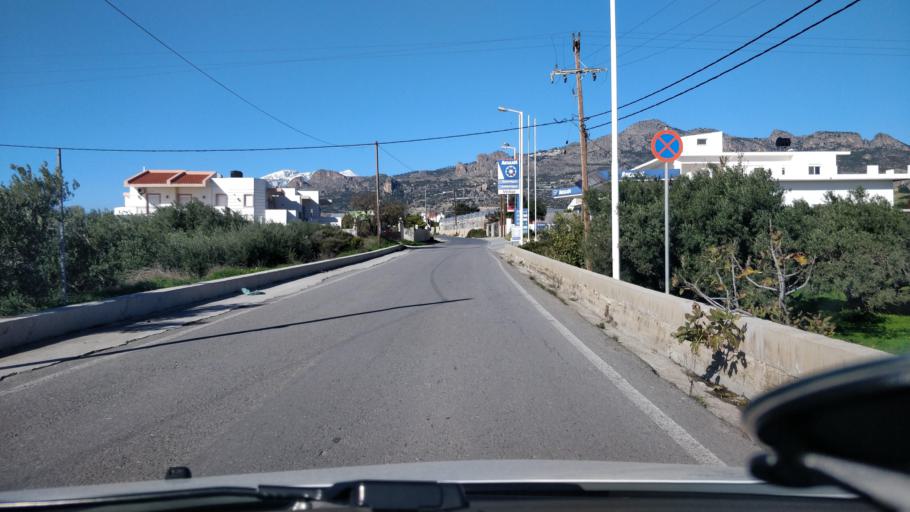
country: GR
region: Crete
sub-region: Nomos Lasithiou
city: Gra Liyia
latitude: 35.0191
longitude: 25.6836
